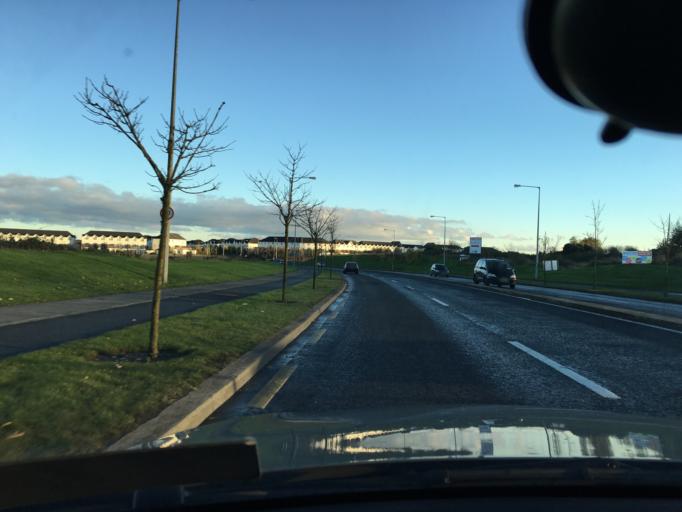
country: IE
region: Leinster
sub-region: Fingal County
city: Swords
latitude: 53.4456
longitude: -6.2181
